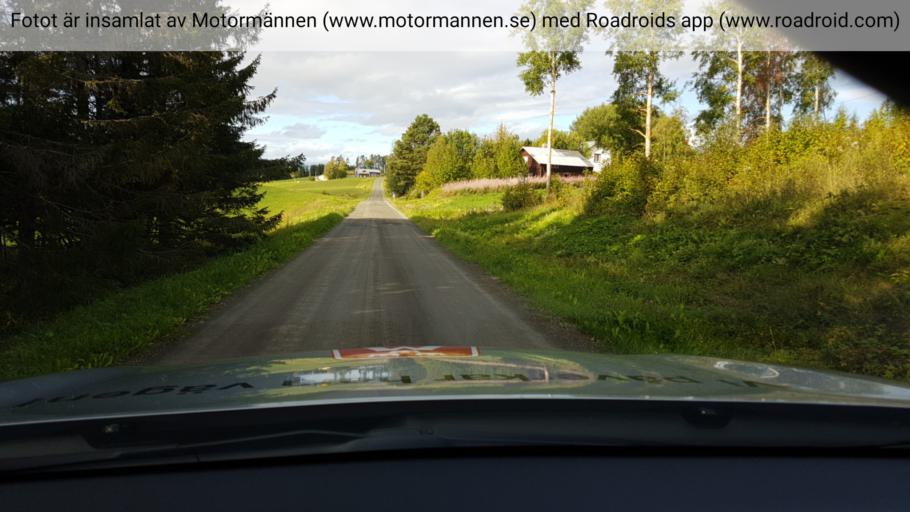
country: SE
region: Jaemtland
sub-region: Bergs Kommun
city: Hoverberg
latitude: 62.9374
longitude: 14.4066
